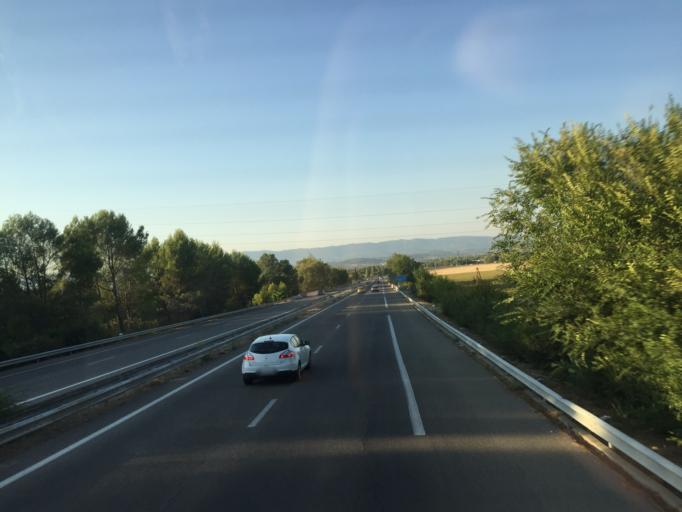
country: FR
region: Provence-Alpes-Cote d'Azur
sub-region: Departement des Bouches-du-Rhone
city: Meyrargues
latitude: 43.6455
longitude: 5.4921
